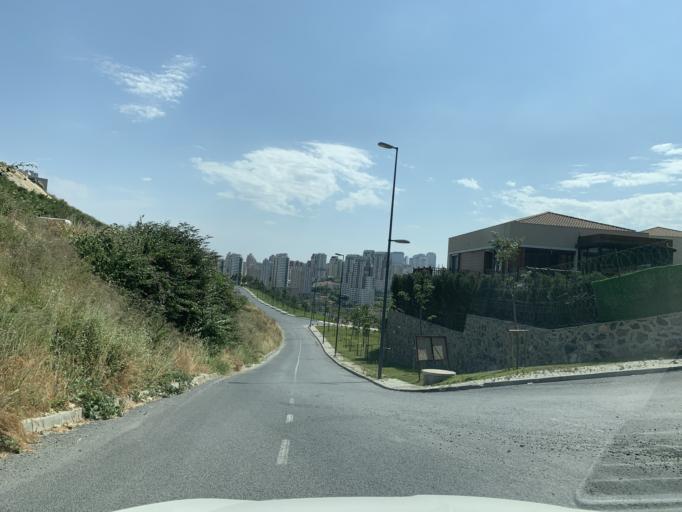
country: TR
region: Istanbul
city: Esenyurt
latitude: 41.0823
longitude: 28.6894
